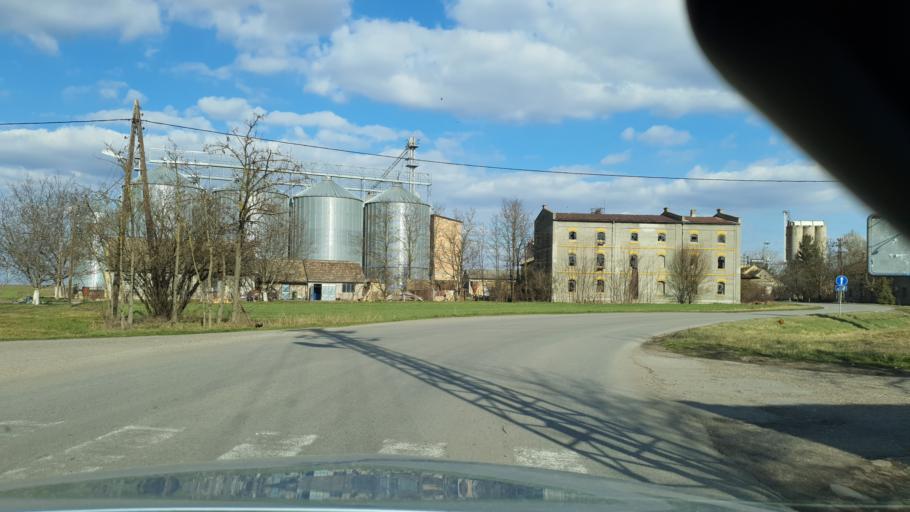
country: RS
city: Ravno Selo
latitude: 45.4520
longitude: 19.6321
